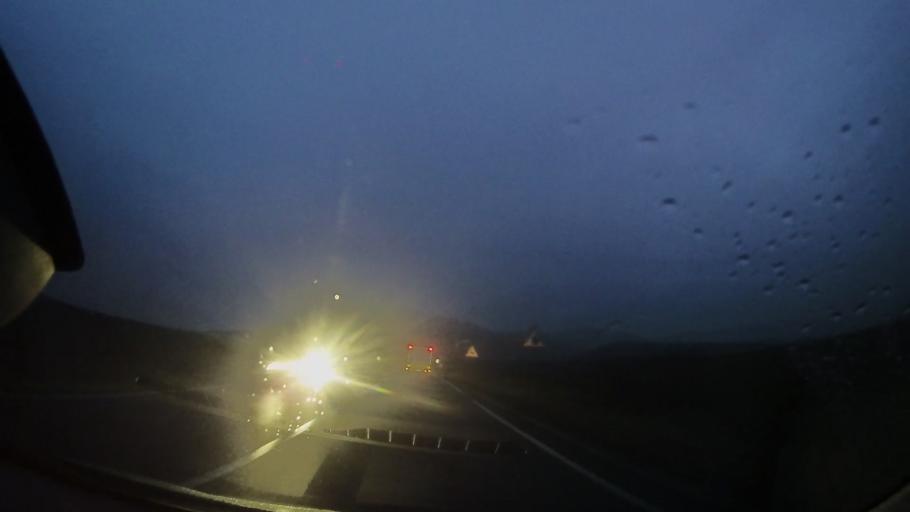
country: RO
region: Harghita
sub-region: Comuna Ditrau
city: Ditrau
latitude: 46.8356
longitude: 25.4903
